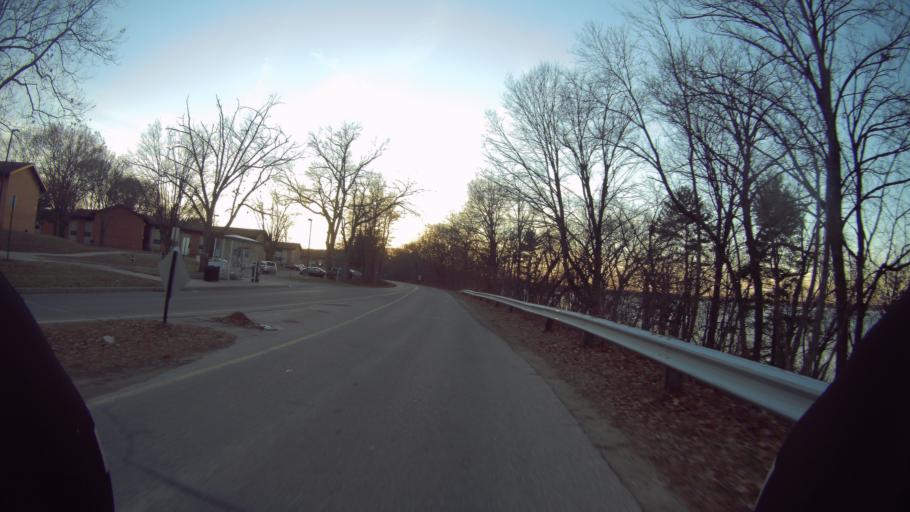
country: US
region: Wisconsin
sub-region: Dane County
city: Shorewood Hills
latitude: 43.0907
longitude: -89.4355
